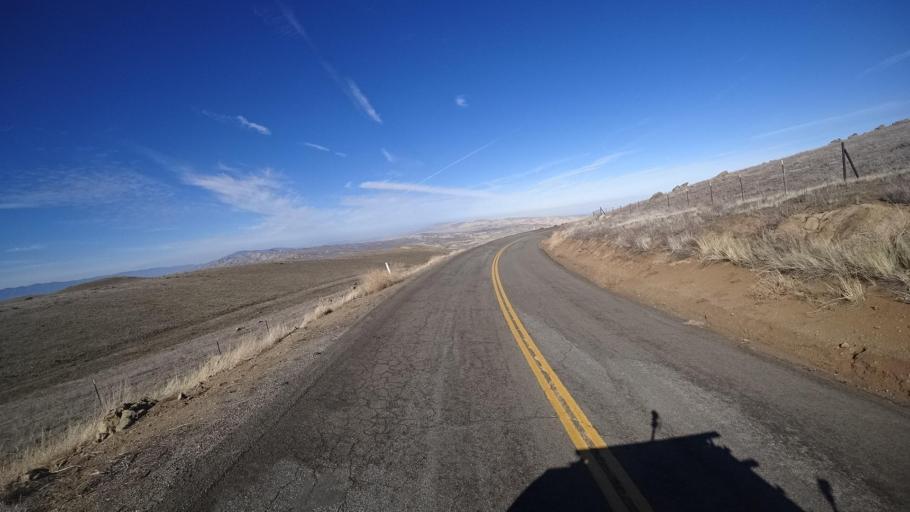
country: US
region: California
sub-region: Kern County
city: Maricopa
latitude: 34.9270
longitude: -119.4125
